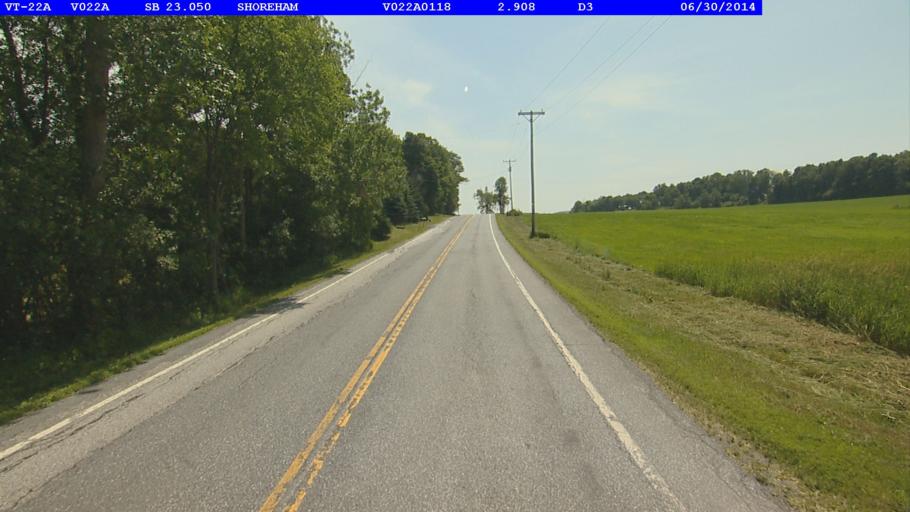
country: US
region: New York
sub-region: Essex County
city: Ticonderoga
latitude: 43.8914
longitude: -73.3093
